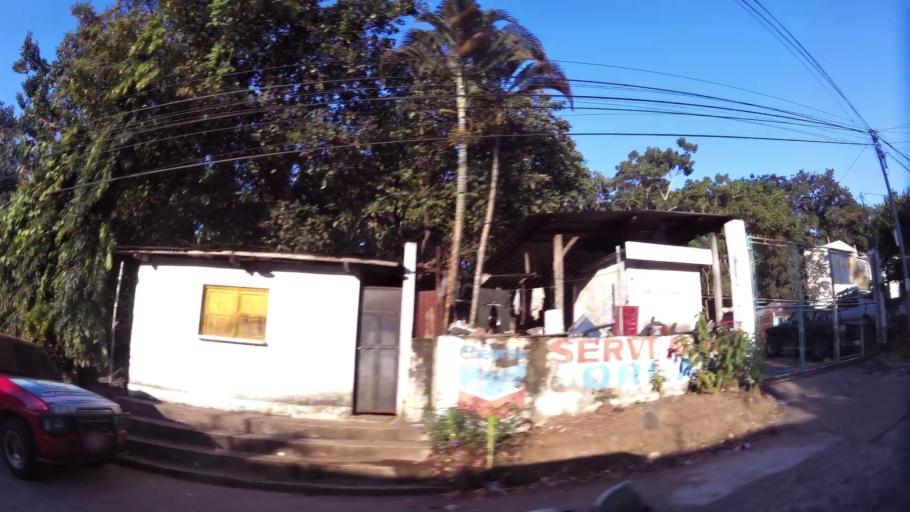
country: GT
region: Suchitepeque
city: Mazatenango
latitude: 14.5394
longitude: -91.5058
